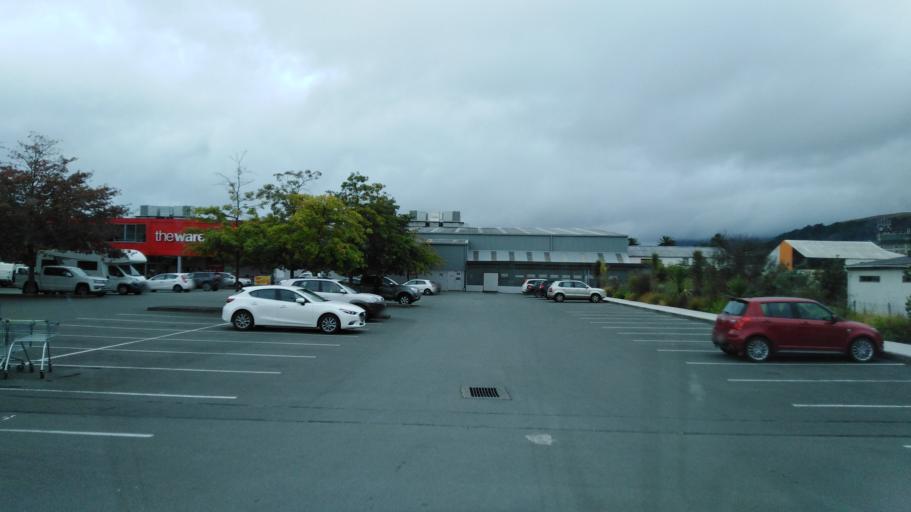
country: NZ
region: Nelson
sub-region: Nelson City
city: Nelson
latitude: -41.2728
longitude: 173.2783
